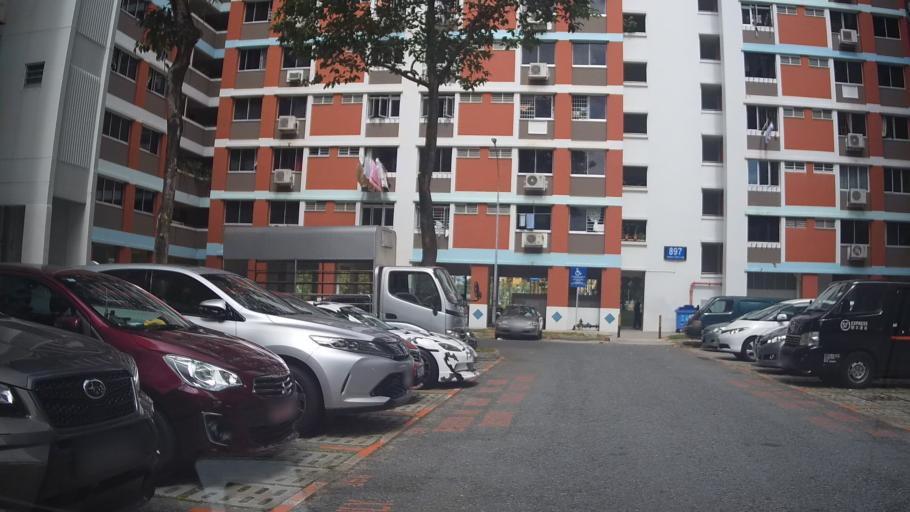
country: SG
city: Singapore
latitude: 1.3476
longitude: 103.9346
